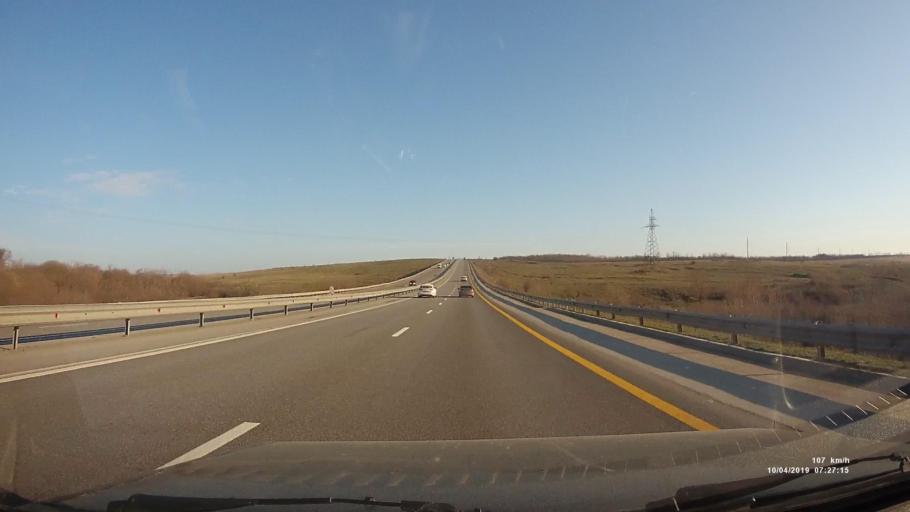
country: RU
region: Rostov
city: Gornyy
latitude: 47.9214
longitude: 40.2184
